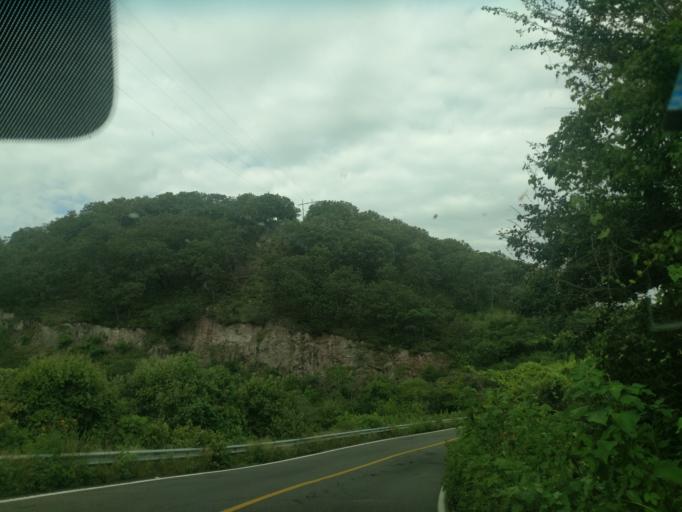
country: MX
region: Jalisco
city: Ameca
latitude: 20.5286
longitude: -104.2320
